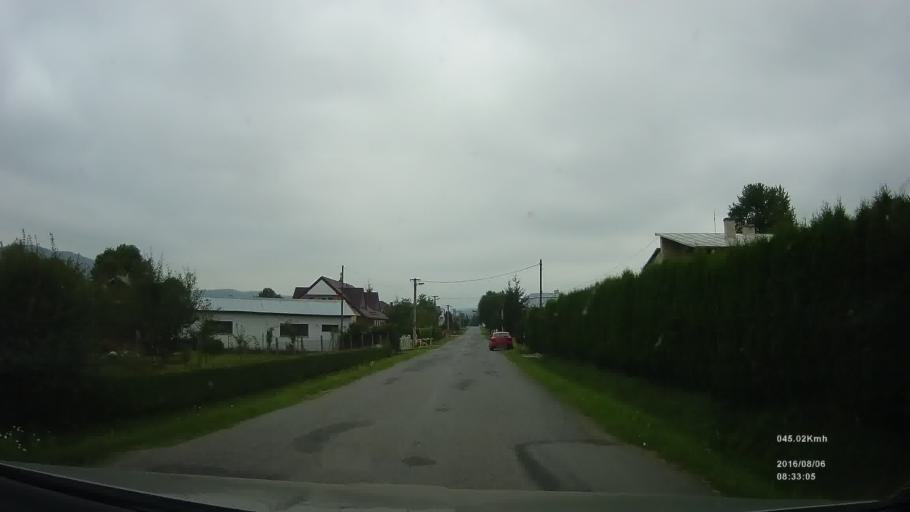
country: SK
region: Presovsky
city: Svidnik
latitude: 49.3410
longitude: 21.5970
